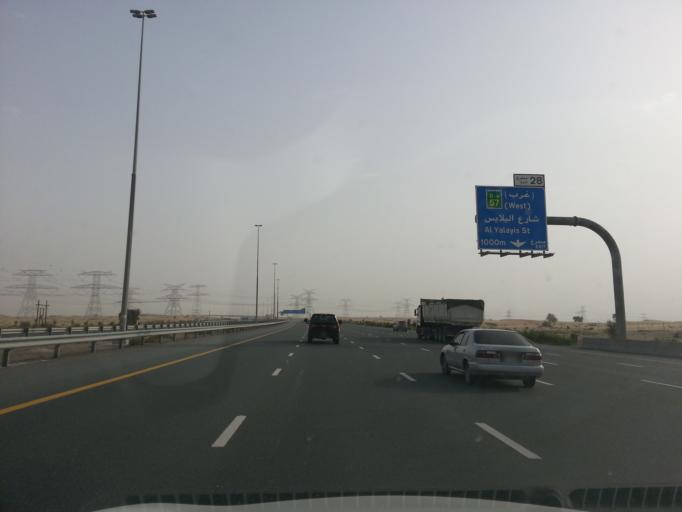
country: AE
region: Dubai
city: Dubai
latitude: 24.9905
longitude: 55.2475
